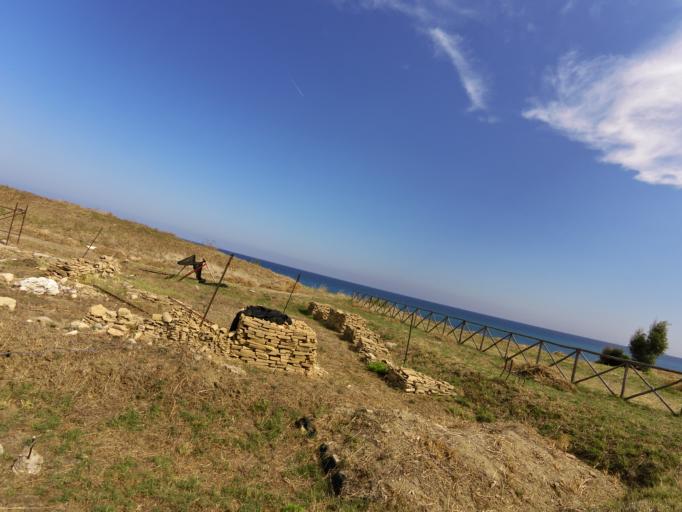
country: IT
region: Calabria
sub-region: Provincia di Reggio Calabria
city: Monasterace Marina
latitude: 38.4464
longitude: 16.5789
